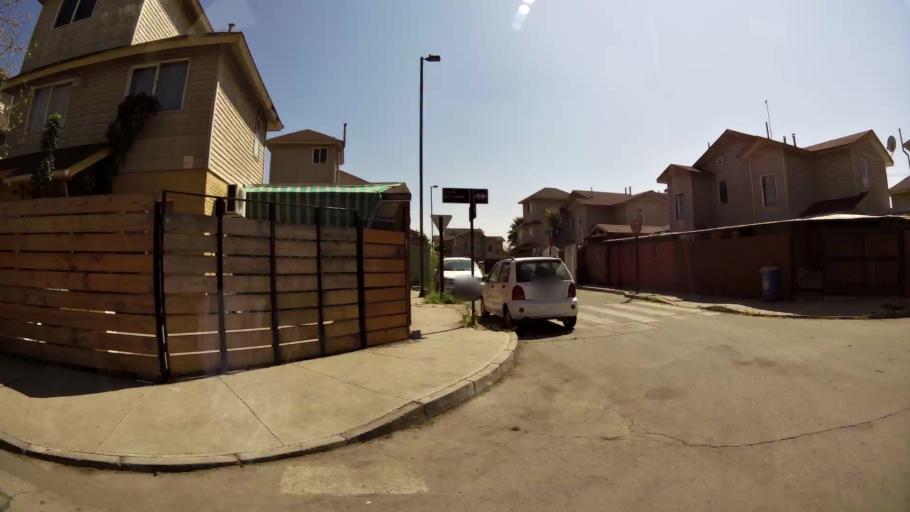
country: CL
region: Santiago Metropolitan
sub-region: Provincia de Chacabuco
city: Chicureo Abajo
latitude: -33.3302
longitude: -70.7492
